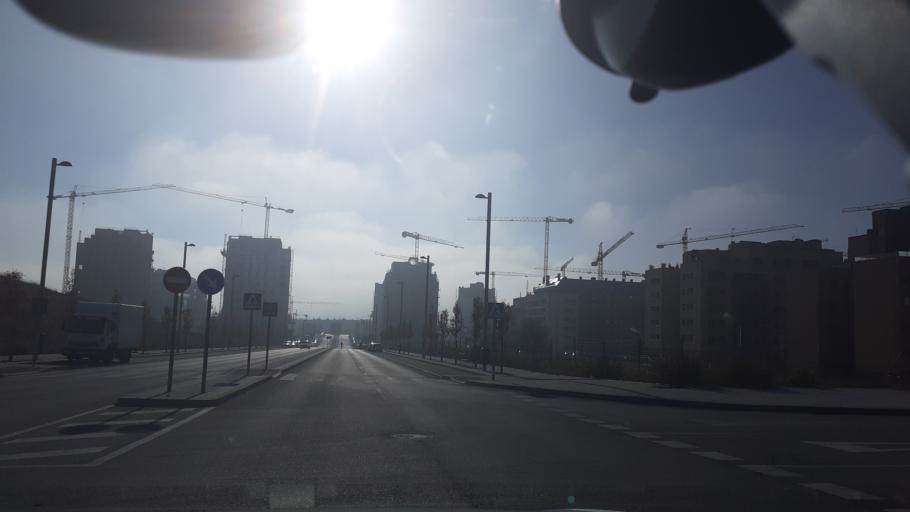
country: ES
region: Madrid
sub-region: Provincia de Madrid
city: Coslada
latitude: 40.4027
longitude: -3.5556
